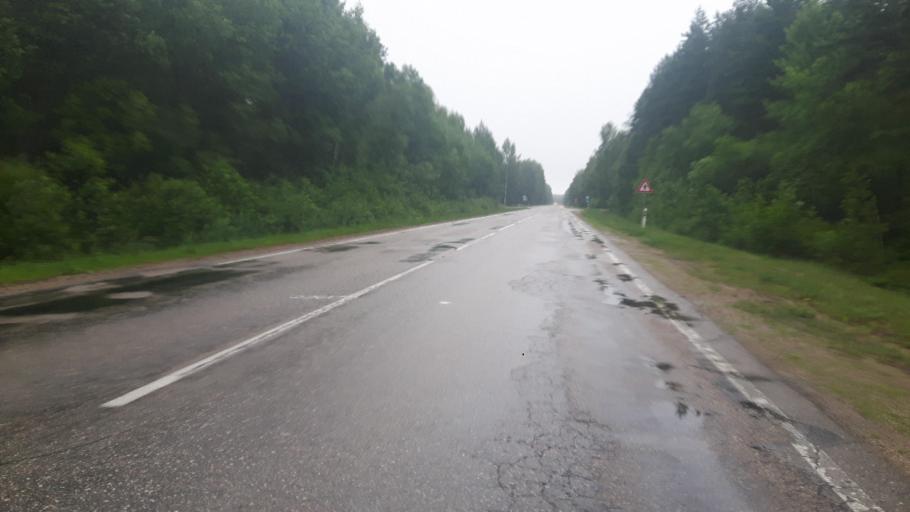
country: LV
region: Rucavas
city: Rucava
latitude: 56.1204
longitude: 21.1447
